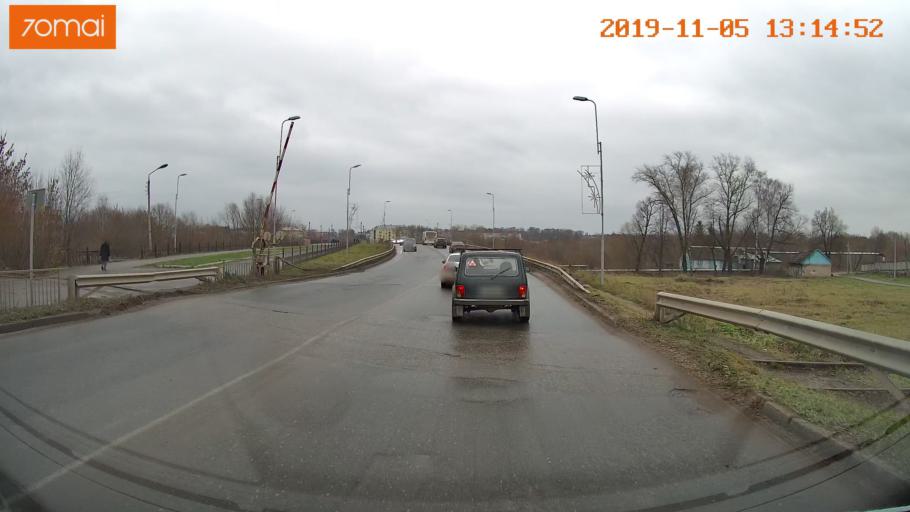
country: RU
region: Ivanovo
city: Shuya
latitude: 56.8510
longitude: 41.3595
